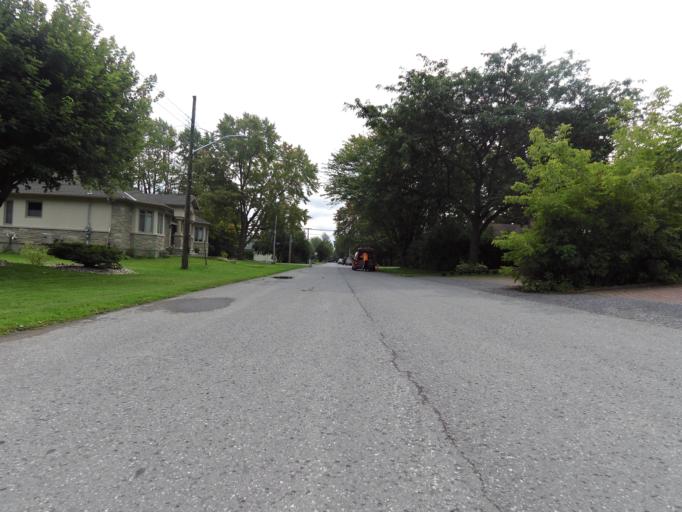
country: CA
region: Ontario
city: Ottawa
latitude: 45.3594
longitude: -75.7072
